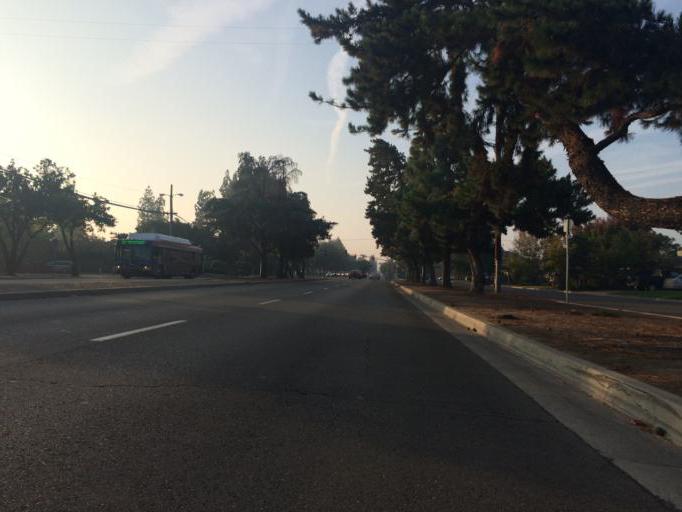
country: US
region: California
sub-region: Fresno County
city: Fresno
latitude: 36.7885
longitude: -119.7726
